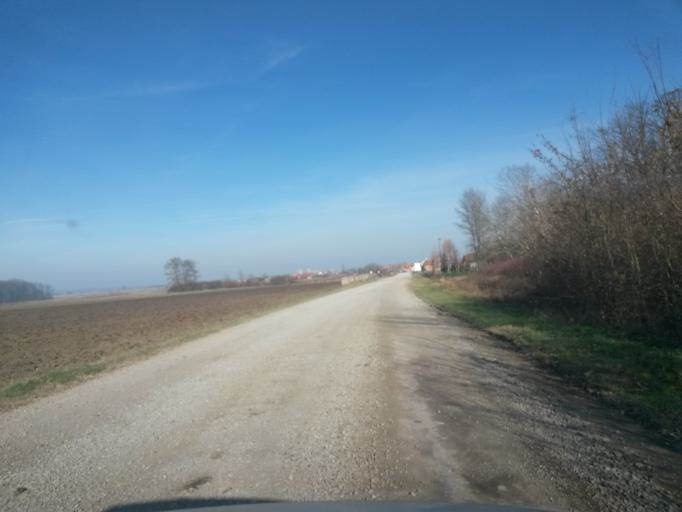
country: HR
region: Vukovarsko-Srijemska
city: Mirkovci
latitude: 45.2324
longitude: 18.8859
